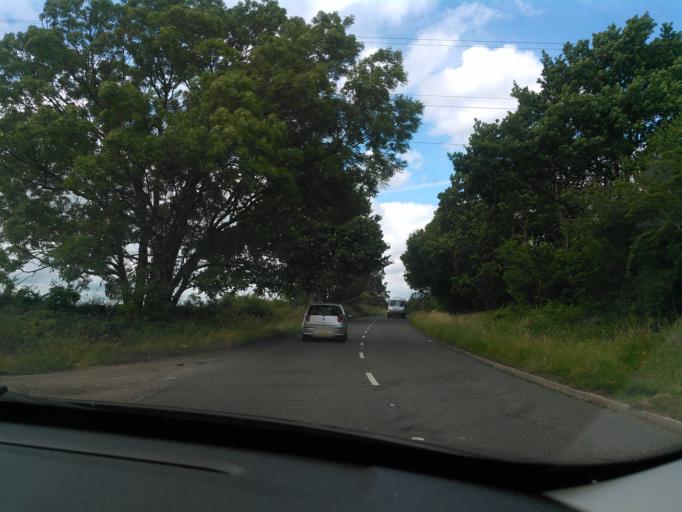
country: GB
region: England
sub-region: Derbyshire
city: Findern
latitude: 52.8595
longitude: -1.5657
